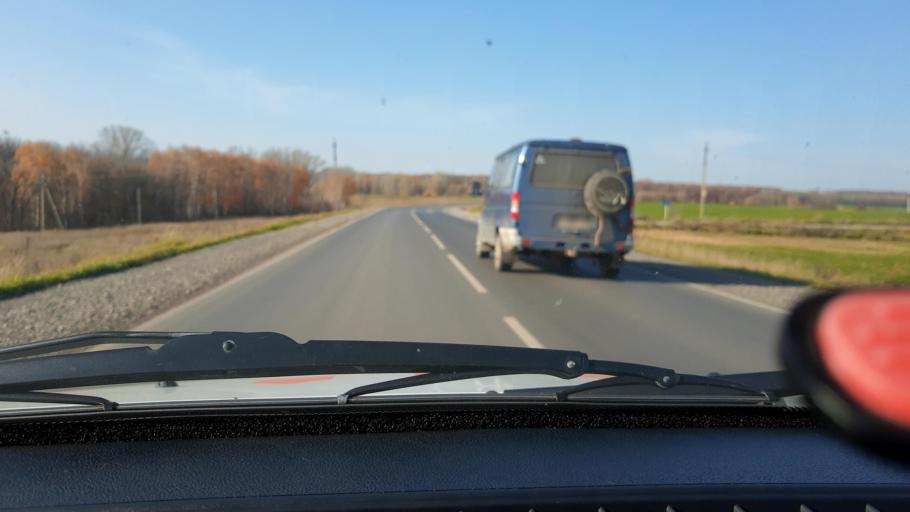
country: RU
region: Bashkortostan
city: Mikhaylovka
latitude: 54.8319
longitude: 55.9463
